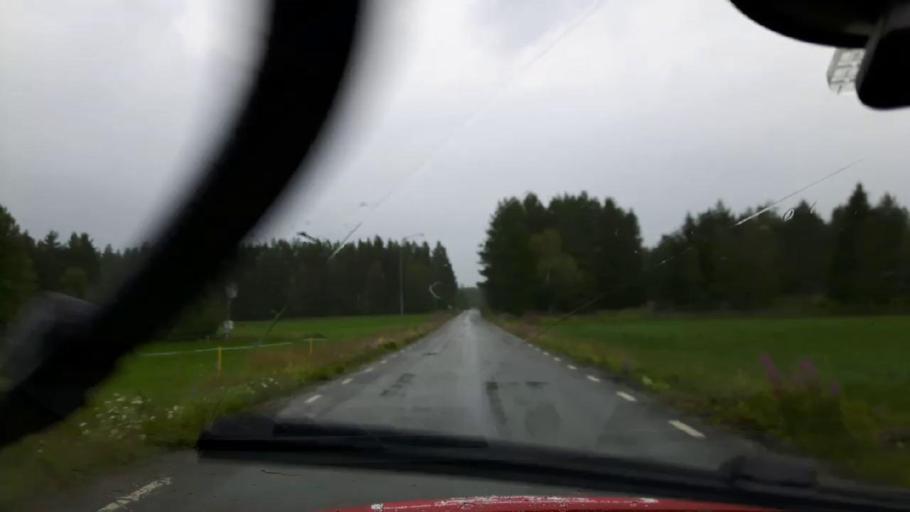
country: SE
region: Jaemtland
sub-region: OEstersunds Kommun
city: Brunflo
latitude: 62.9837
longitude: 14.8179
